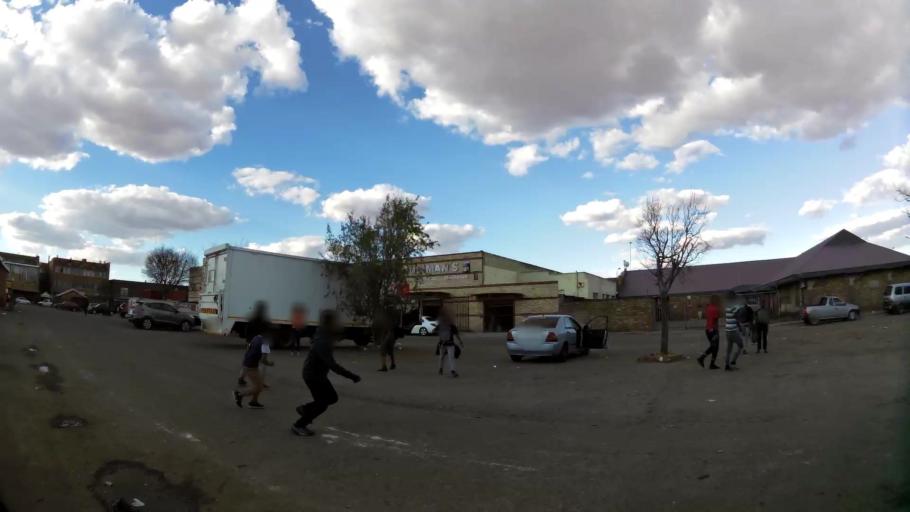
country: ZA
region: North-West
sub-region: Dr Kenneth Kaunda District Municipality
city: Potchefstroom
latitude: -26.7133
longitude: 27.0985
